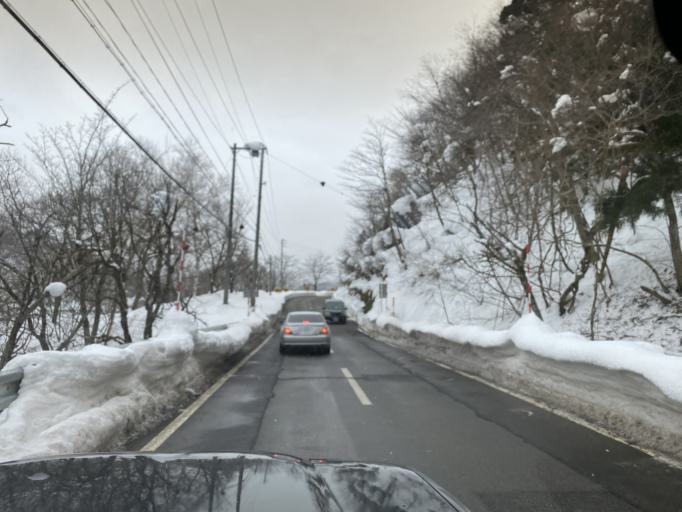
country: JP
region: Gifu
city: Takayama
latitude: 36.0975
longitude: 136.9353
